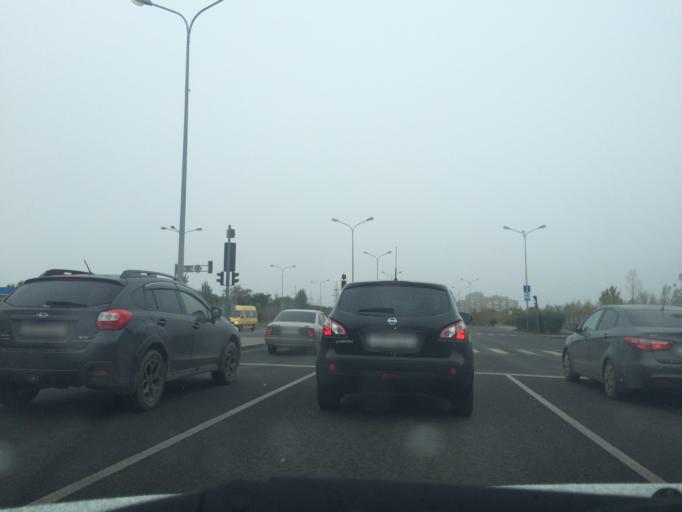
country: KZ
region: Astana Qalasy
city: Astana
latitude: 51.1865
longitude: 71.3542
